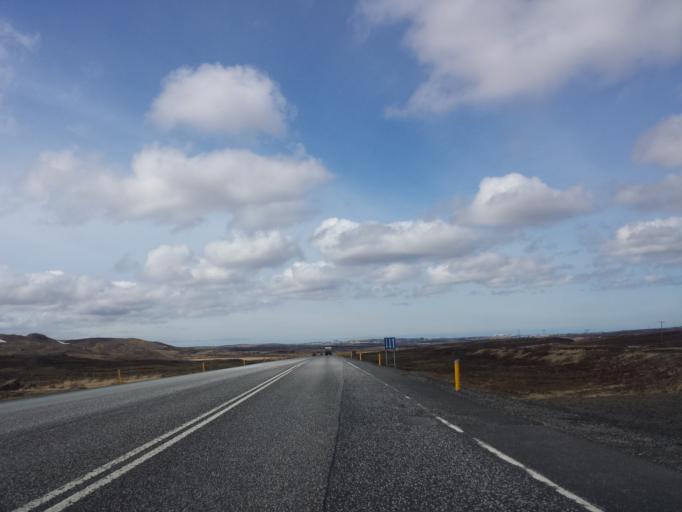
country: IS
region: Capital Region
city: Mosfellsbaer
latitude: 64.0714
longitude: -21.6198
